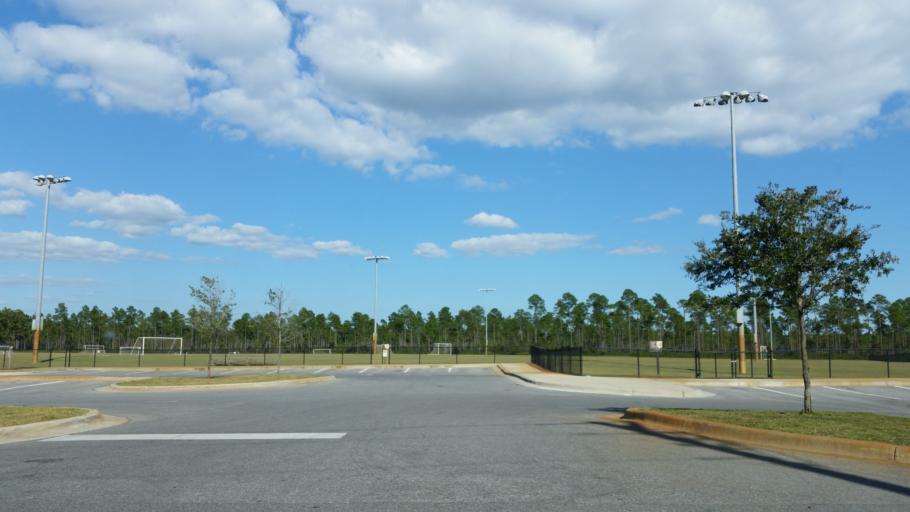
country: US
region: Florida
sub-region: Escambia County
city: Myrtle Grove
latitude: 30.3859
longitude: -87.3939
